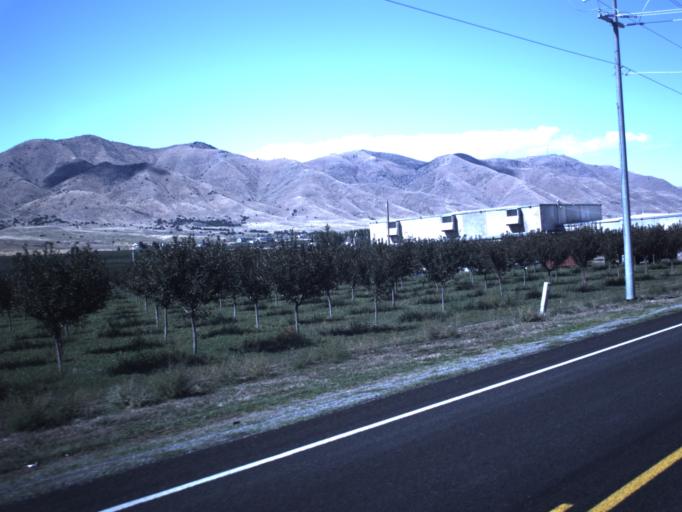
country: US
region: Utah
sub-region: Utah County
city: West Mountain
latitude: 40.0312
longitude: -111.7871
